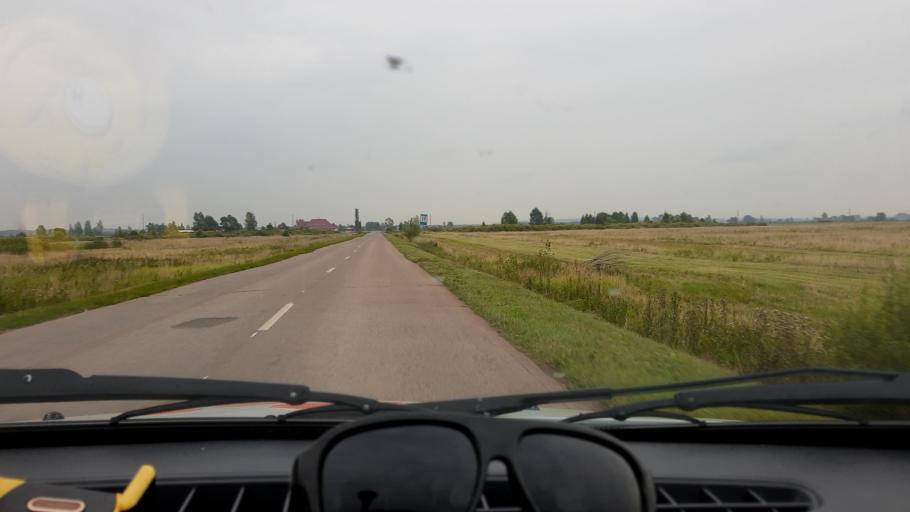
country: RU
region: Bashkortostan
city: Blagoveshchensk
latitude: 54.9912
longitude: 55.7672
